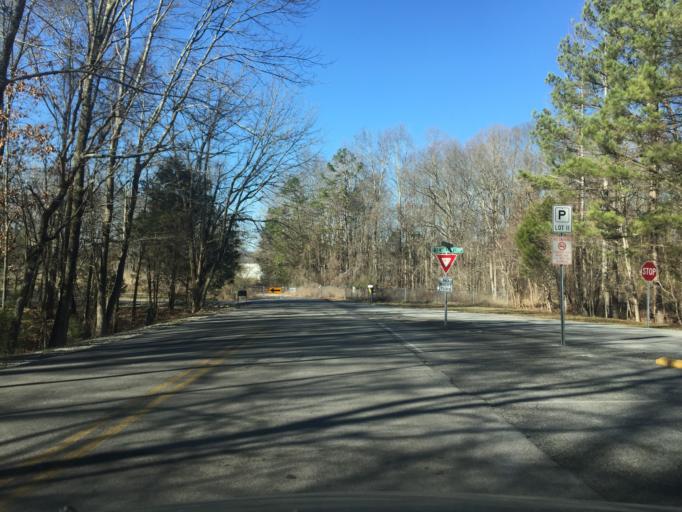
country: US
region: Tennessee
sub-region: Hamilton County
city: Harrison
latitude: 35.0870
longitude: -85.1275
